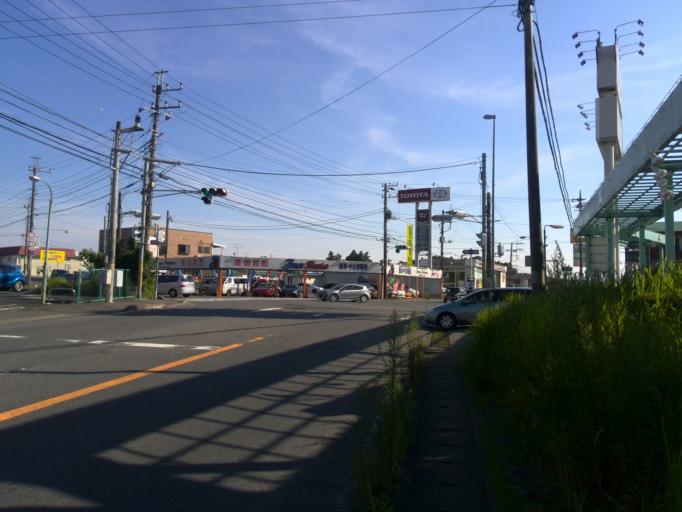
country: JP
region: Chiba
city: Narita
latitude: 35.7552
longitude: 140.3033
